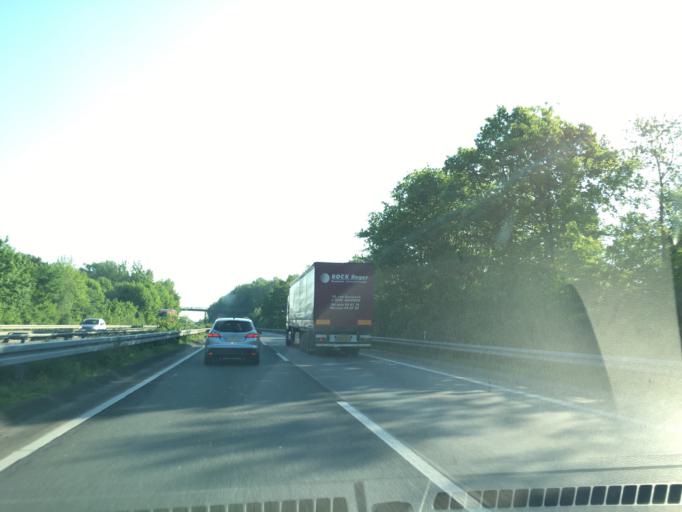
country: DE
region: Lower Saxony
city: Hasbergen
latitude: 52.2480
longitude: 7.9089
